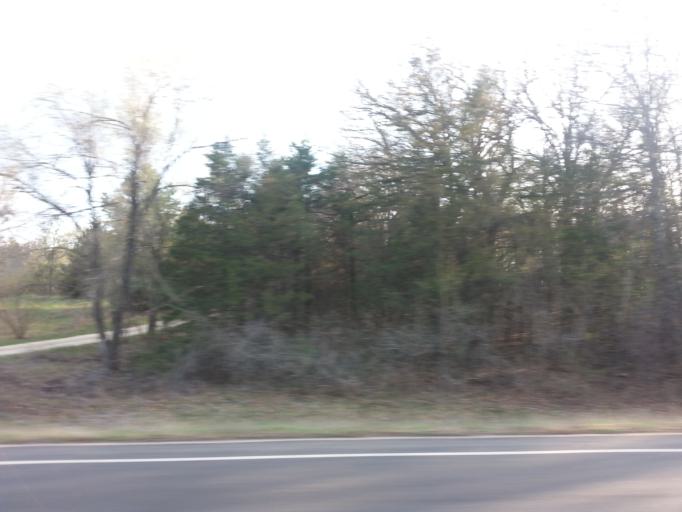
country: US
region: Wisconsin
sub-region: Pierce County
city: River Falls
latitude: 44.8316
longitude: -92.6354
